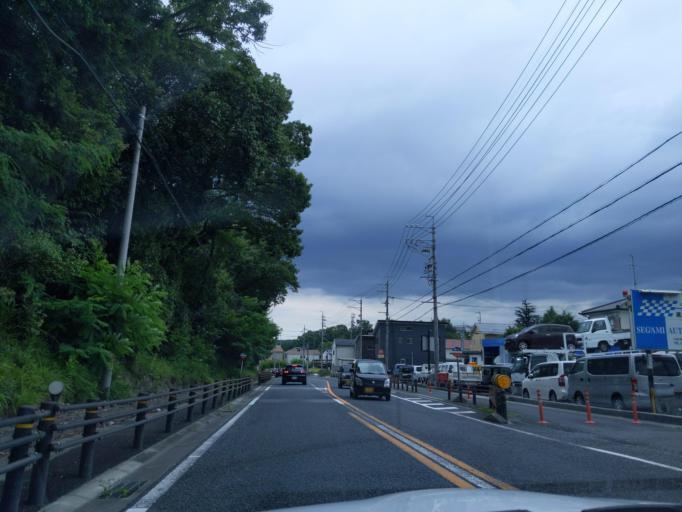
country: JP
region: Aichi
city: Seto
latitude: 35.2067
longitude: 137.1028
